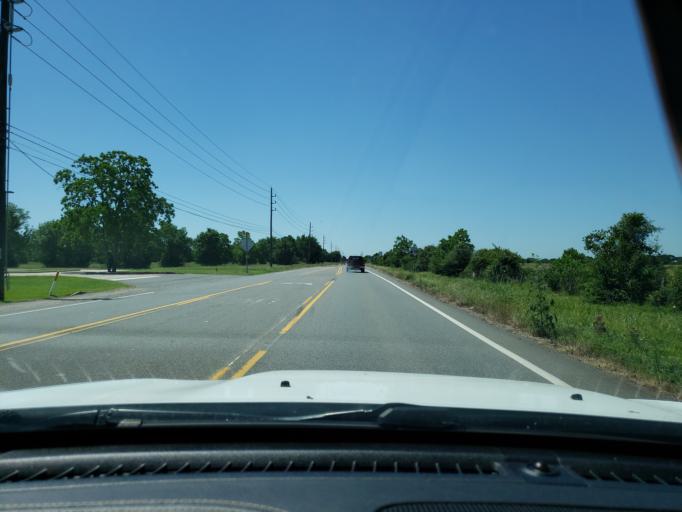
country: US
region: Texas
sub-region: Fort Bend County
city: Fulshear
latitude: 29.6932
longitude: -95.8460
